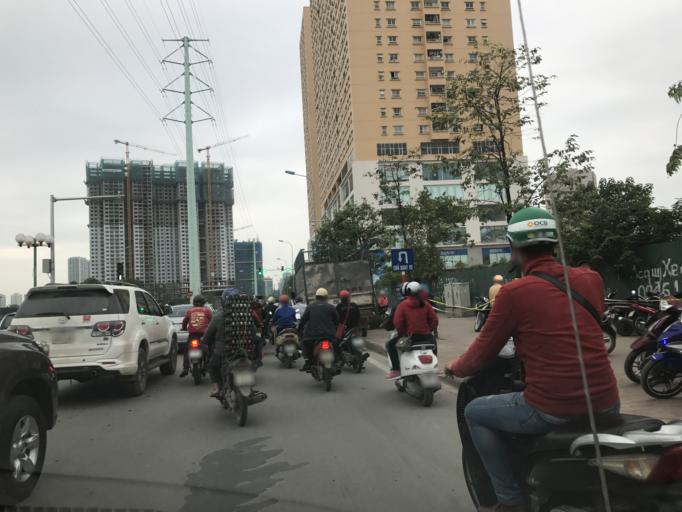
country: VN
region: Ha Noi
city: Thanh Xuan
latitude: 20.9902
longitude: 105.7828
